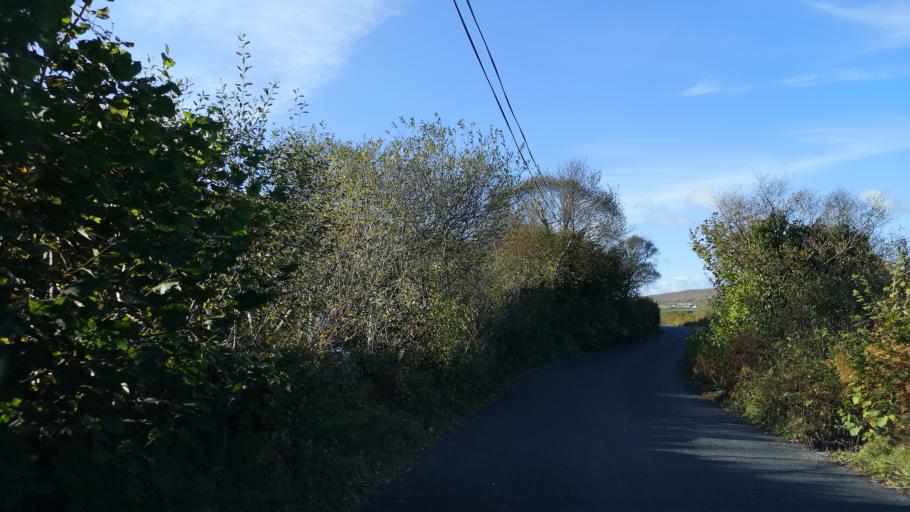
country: IE
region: Connaught
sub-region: County Galway
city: Clifden
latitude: 53.5033
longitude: -10.0630
